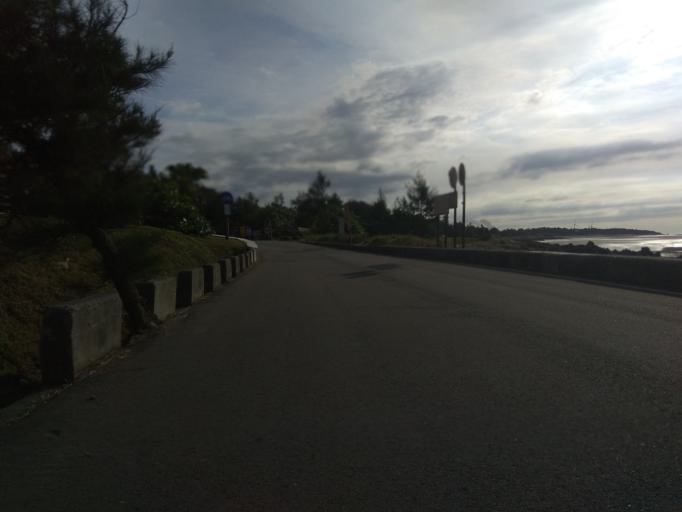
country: TW
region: Taiwan
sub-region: Hsinchu
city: Zhubei
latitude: 24.9599
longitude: 121.0033
